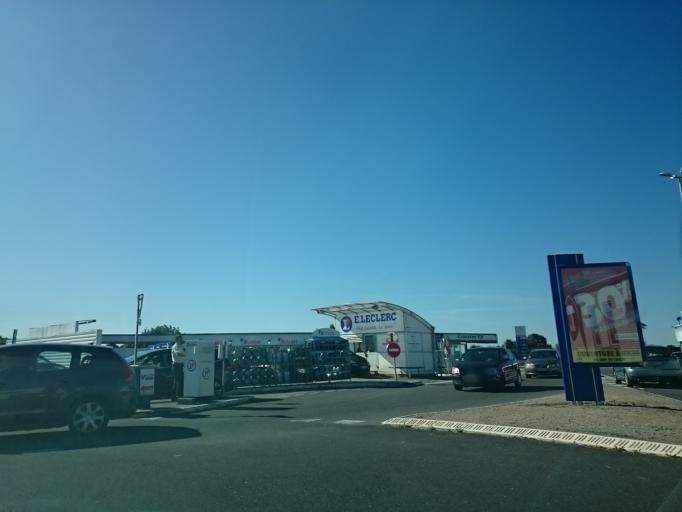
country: FR
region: Brittany
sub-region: Departement du Finistere
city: Gouesnou
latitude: 48.4297
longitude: -4.4715
